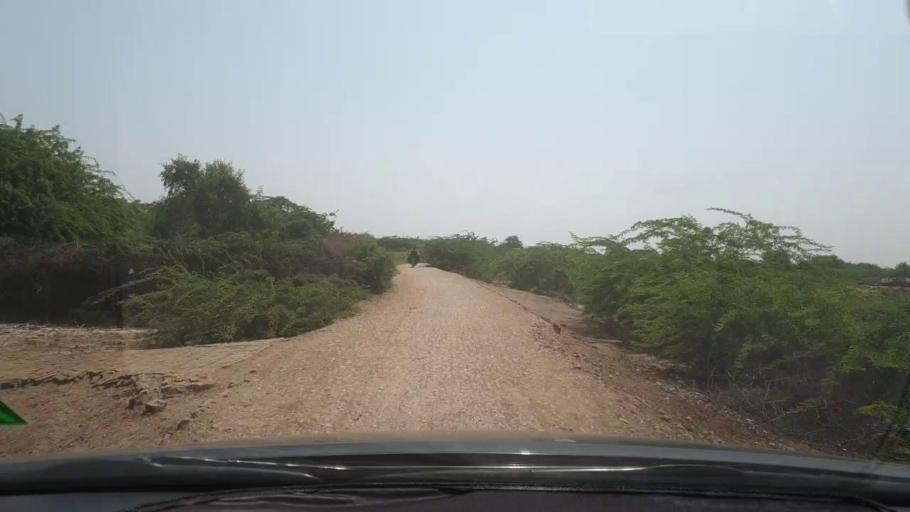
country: PK
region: Sindh
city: Tando Bago
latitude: 24.8029
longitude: 69.1834
